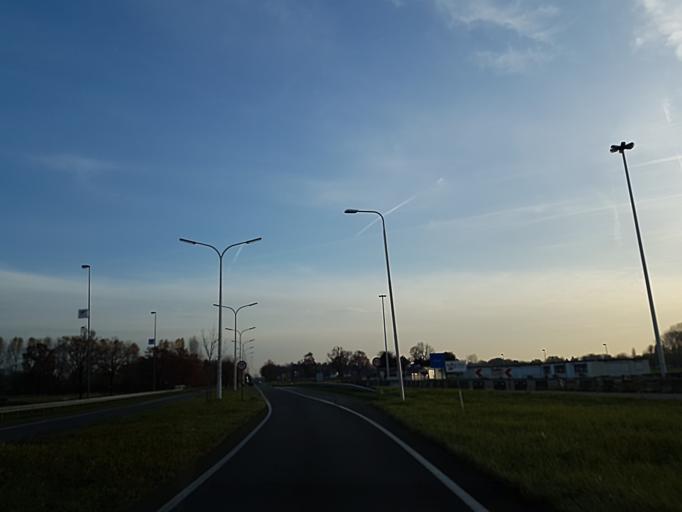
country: BE
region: Flanders
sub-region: Provincie Antwerpen
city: Essen
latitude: 51.4780
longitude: 4.4742
